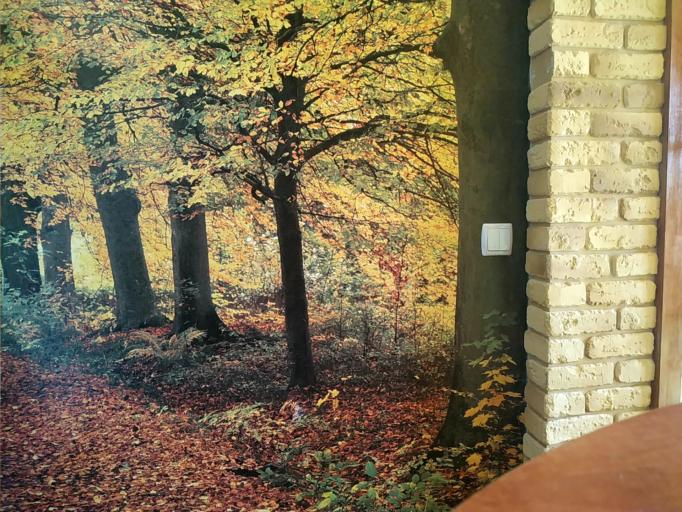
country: RU
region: Jaroslavl
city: Kukoboy
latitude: 58.9068
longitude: 39.6881
